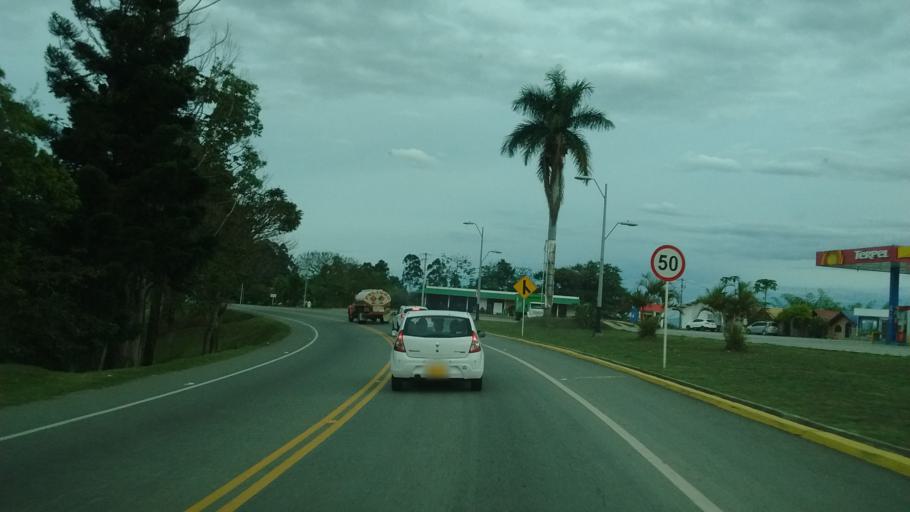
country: CO
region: Cauca
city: Cajibio
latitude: 2.6990
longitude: -76.5338
